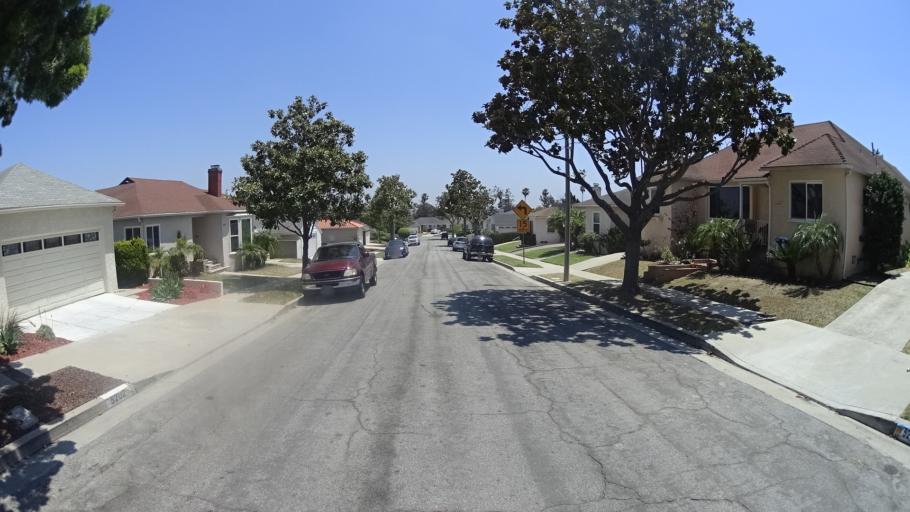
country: US
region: California
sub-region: Los Angeles County
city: View Park-Windsor Hills
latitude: 33.9946
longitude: -118.3476
